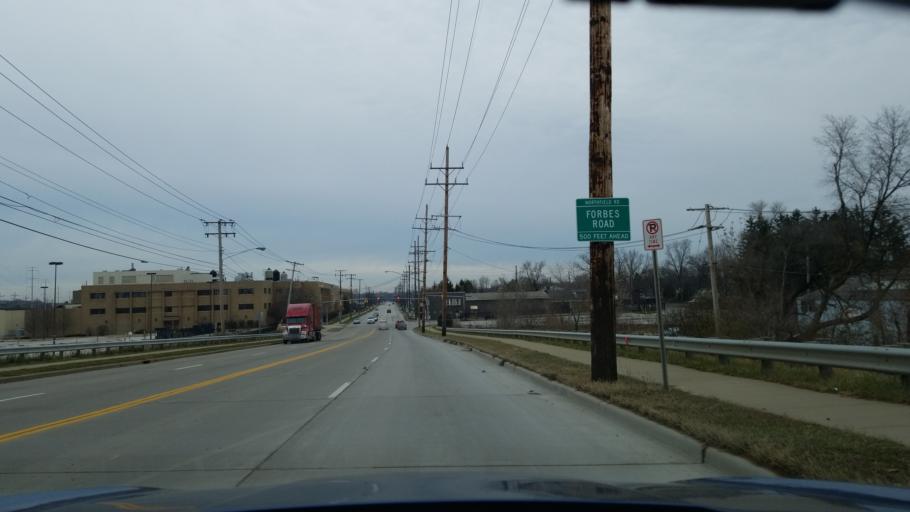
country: US
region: Ohio
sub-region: Cuyahoga County
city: Oakwood
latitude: 41.3712
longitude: -81.5268
